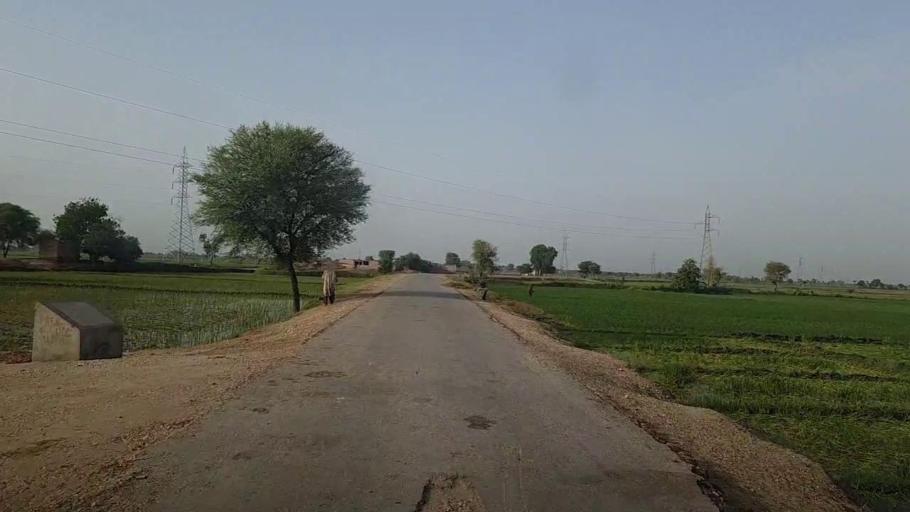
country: PK
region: Sindh
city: Mehar
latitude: 27.1448
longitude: 67.7958
